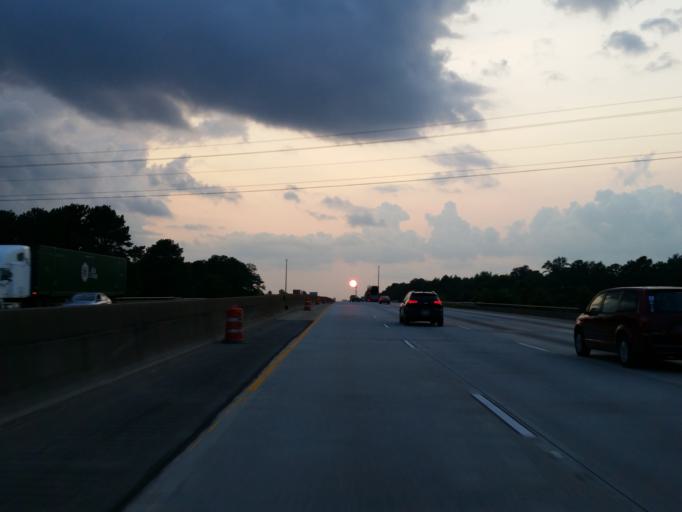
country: US
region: Georgia
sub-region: Henry County
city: Stockbridge
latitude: 33.5466
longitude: -84.2778
